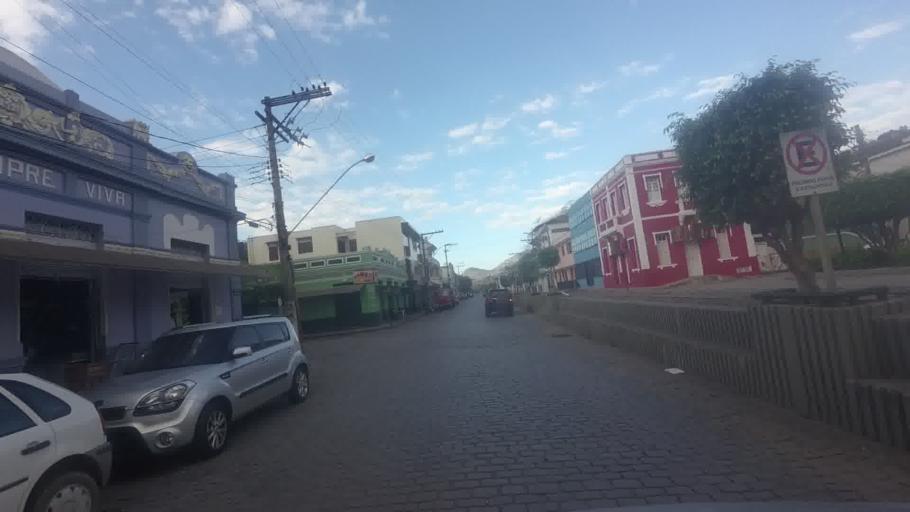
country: BR
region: Espirito Santo
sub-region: Mimoso Do Sul
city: Mimoso do Sul
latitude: -20.9506
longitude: -41.3446
